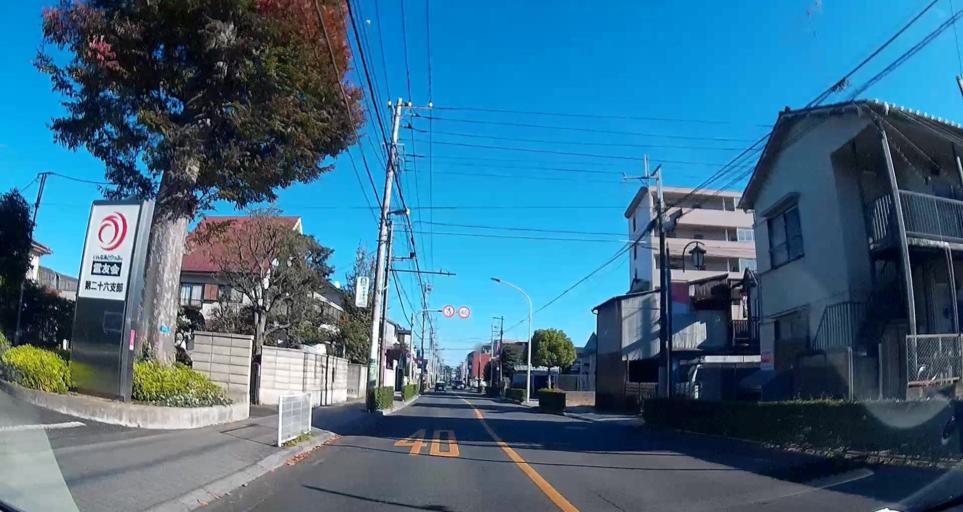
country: JP
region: Tokyo
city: Mitaka-shi
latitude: 35.6823
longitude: 139.5712
